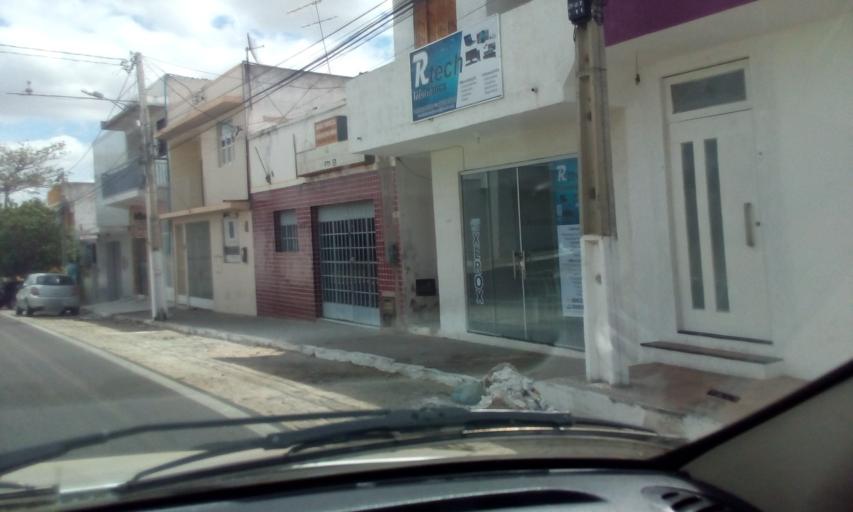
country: BR
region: Rio Grande do Norte
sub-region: Currais Novos
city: Currais Novos
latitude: -6.2622
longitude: -36.5167
